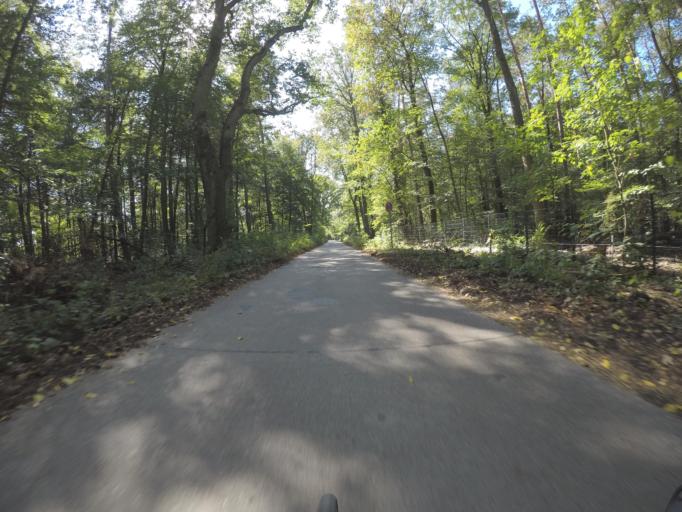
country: DE
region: Berlin
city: Konradshohe
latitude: 52.5869
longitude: 13.2544
